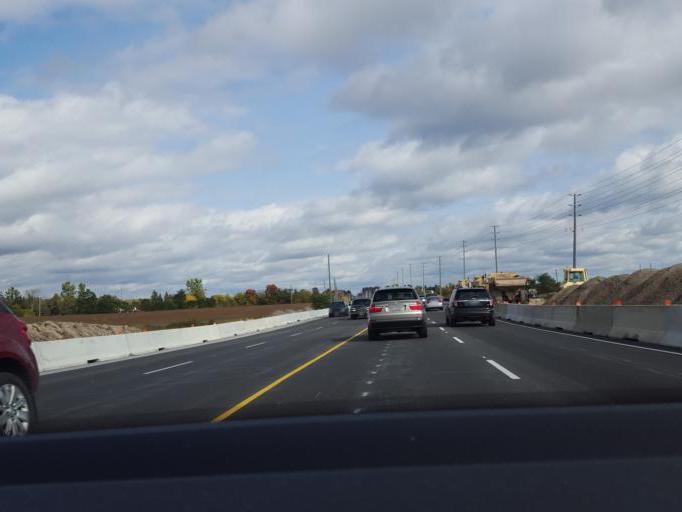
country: CA
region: Ontario
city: Ajax
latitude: 43.9072
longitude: -78.9920
